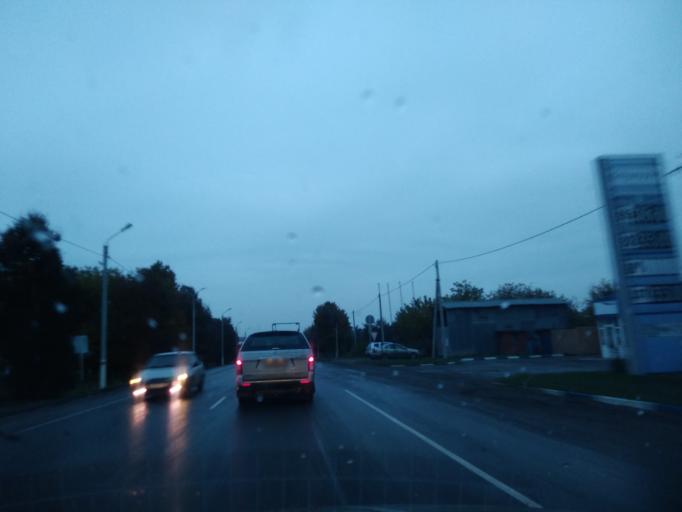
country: RU
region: Tula
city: Teploye
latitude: 53.6158
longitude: 37.5985
